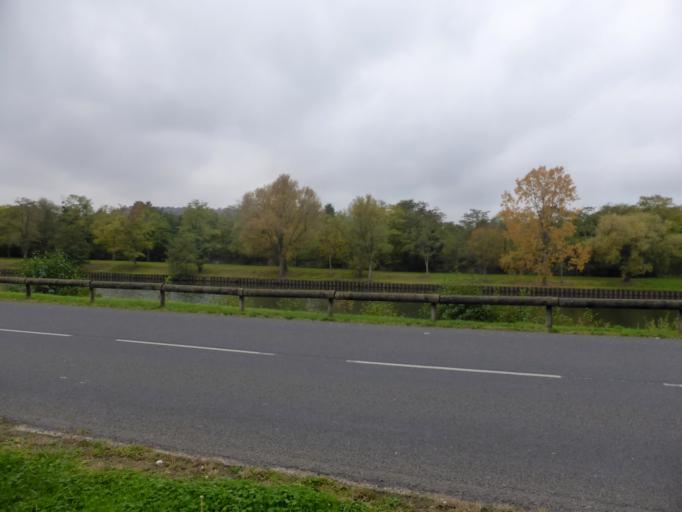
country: FR
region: Lorraine
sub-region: Departement de Meurthe-et-Moselle
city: Frouard
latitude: 48.7659
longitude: 6.1353
